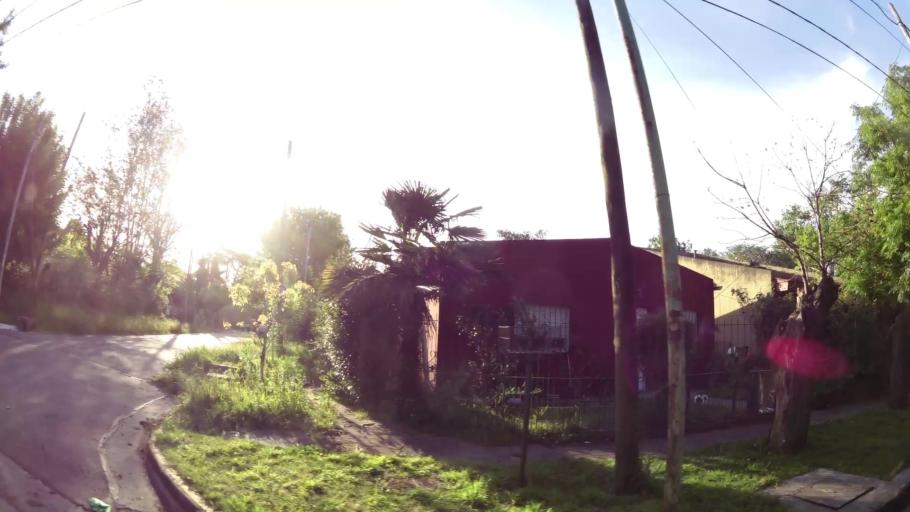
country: AR
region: Buenos Aires
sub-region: Partido de Quilmes
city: Quilmes
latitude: -34.7819
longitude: -58.1995
